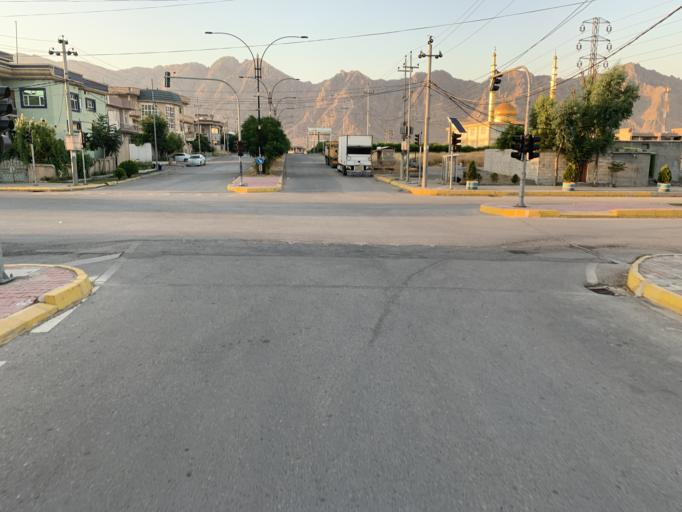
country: IQ
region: As Sulaymaniyah
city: Raniye
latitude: 36.2456
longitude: 44.8782
